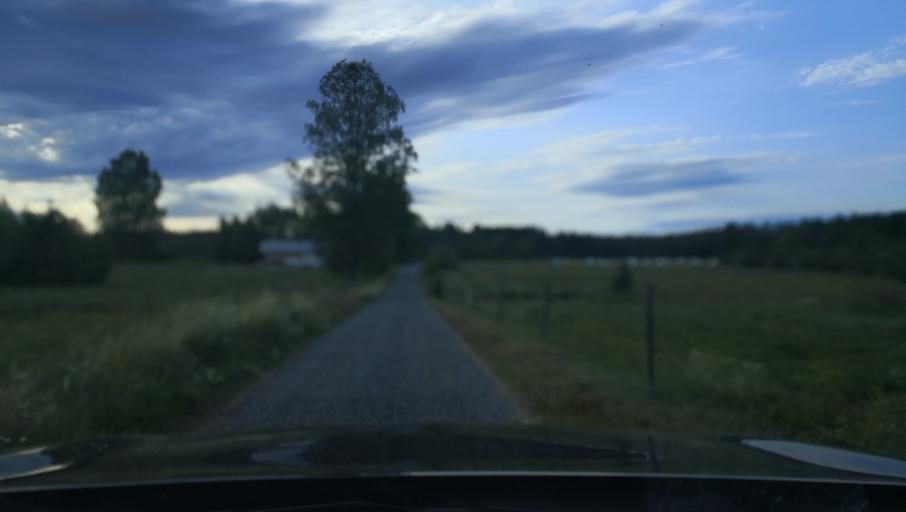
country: SE
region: Dalarna
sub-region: Ludvika Kommun
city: Ludvika
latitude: 60.0753
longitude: 15.2591
